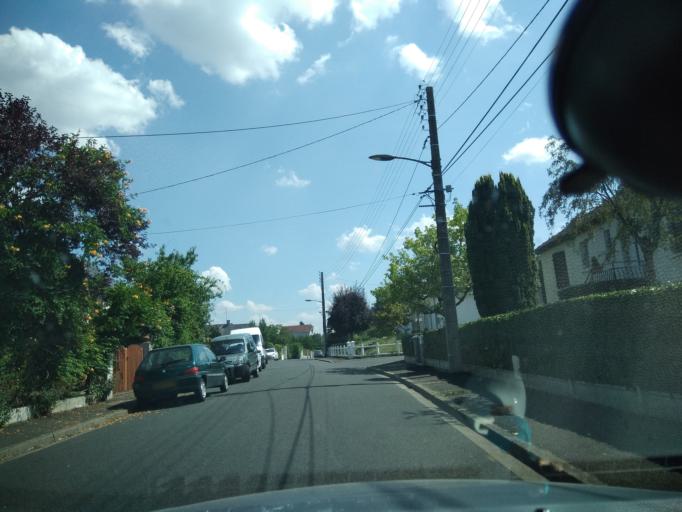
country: FR
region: Centre
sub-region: Departement d'Indre-et-Loire
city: Chambray-les-Tours
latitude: 47.3535
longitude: 0.6930
